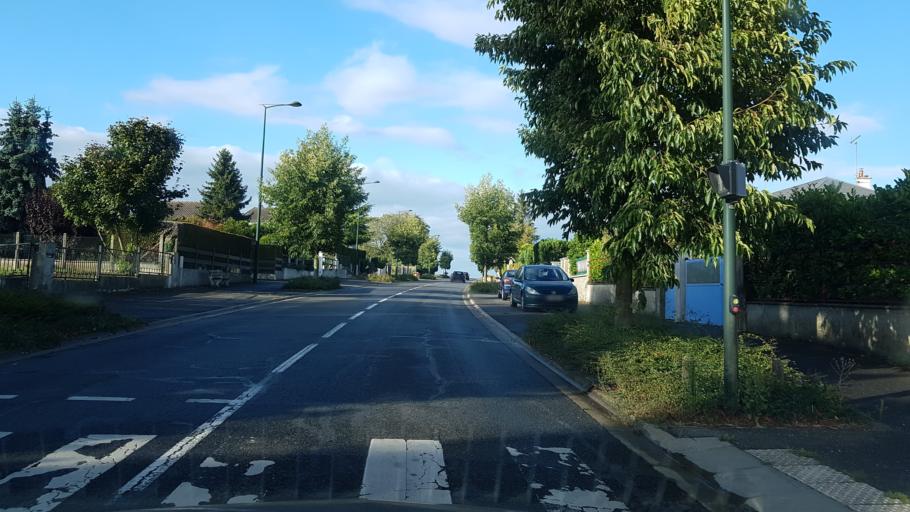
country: FR
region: Centre
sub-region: Departement du Loiret
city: Sermaises
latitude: 48.2990
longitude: 2.2002
